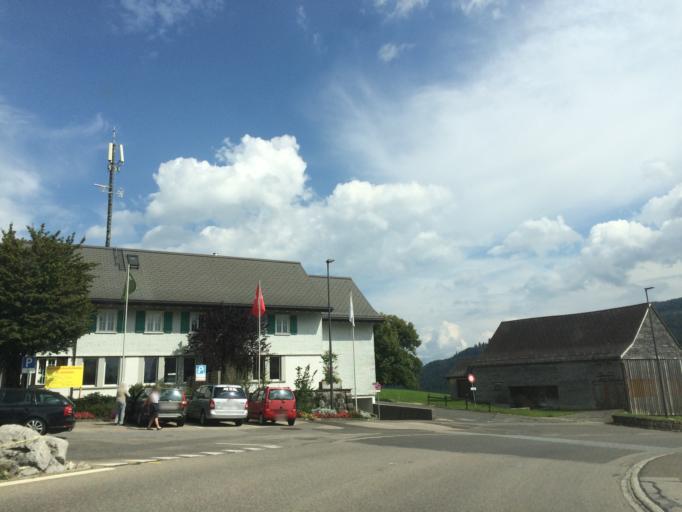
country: CH
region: Saint Gallen
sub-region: Wahlkreis Toggenburg
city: Wildhaus
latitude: 47.2033
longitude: 9.3505
